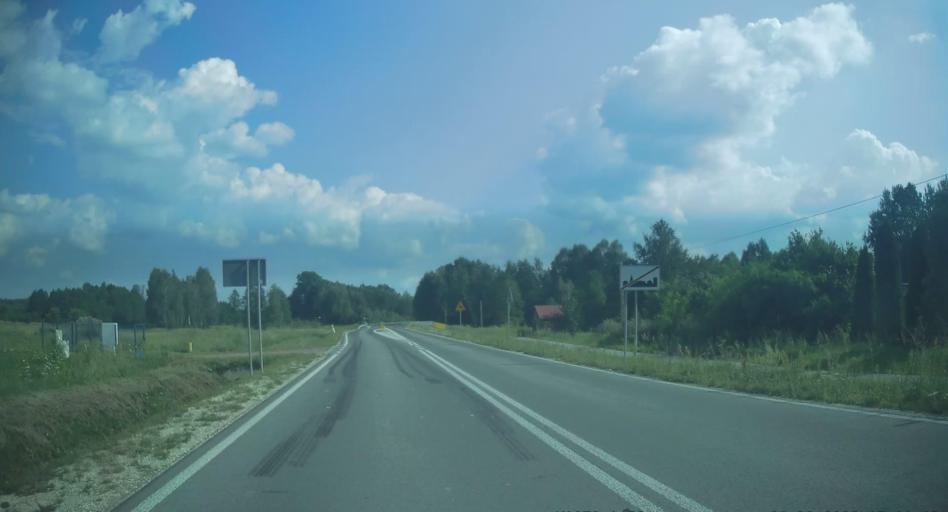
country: PL
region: Swietokrzyskie
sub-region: Powiat konecki
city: Radoszyce
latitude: 51.0617
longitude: 20.2758
